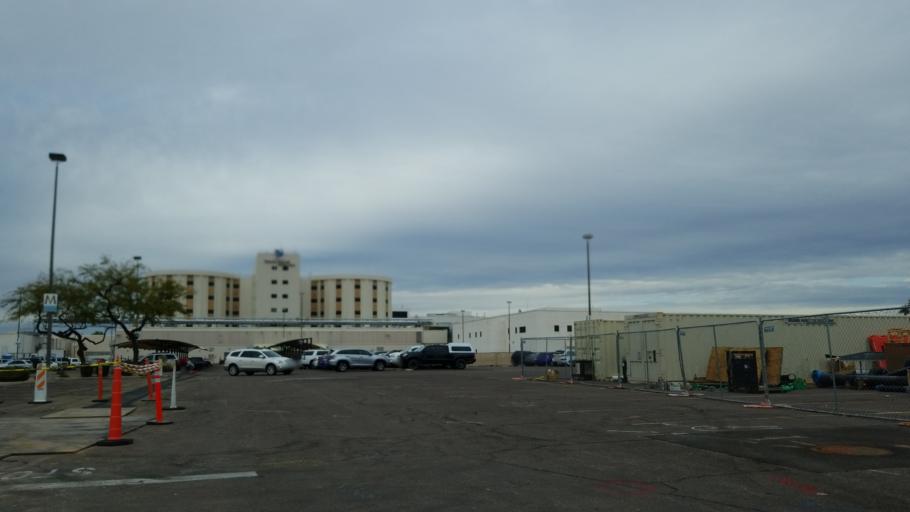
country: US
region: Arizona
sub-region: Maricopa County
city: Sun City
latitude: 33.6016
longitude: -112.2838
